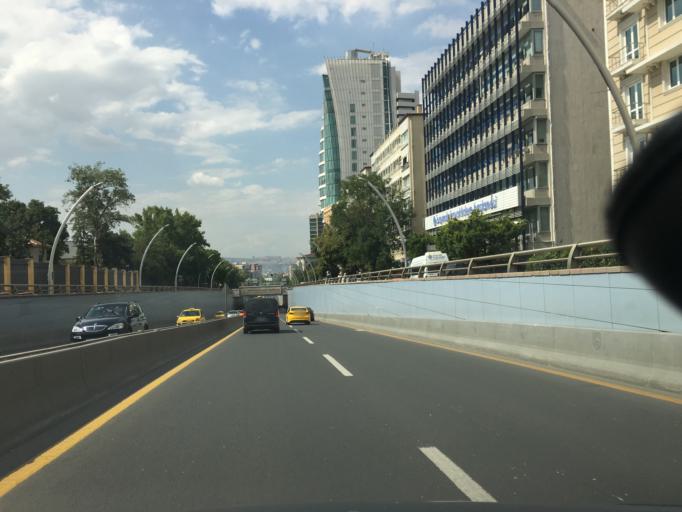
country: TR
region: Ankara
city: Cankaya
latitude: 39.9069
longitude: 32.8574
